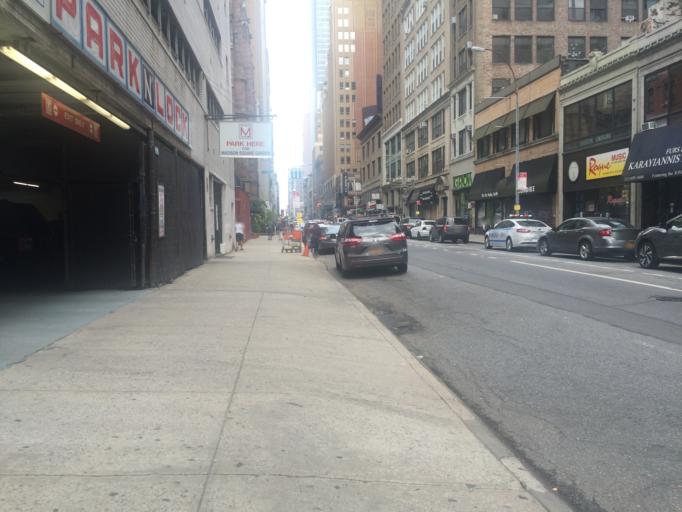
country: US
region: New Jersey
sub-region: Hudson County
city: Weehawken
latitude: 40.7490
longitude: -73.9937
